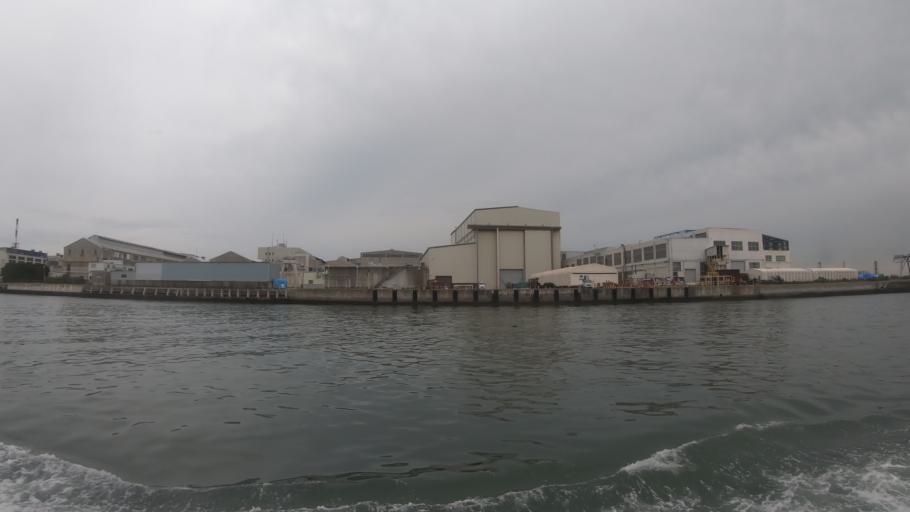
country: JP
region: Kanagawa
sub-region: Kawasaki-shi
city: Kawasaki
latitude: 35.4852
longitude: 139.6945
